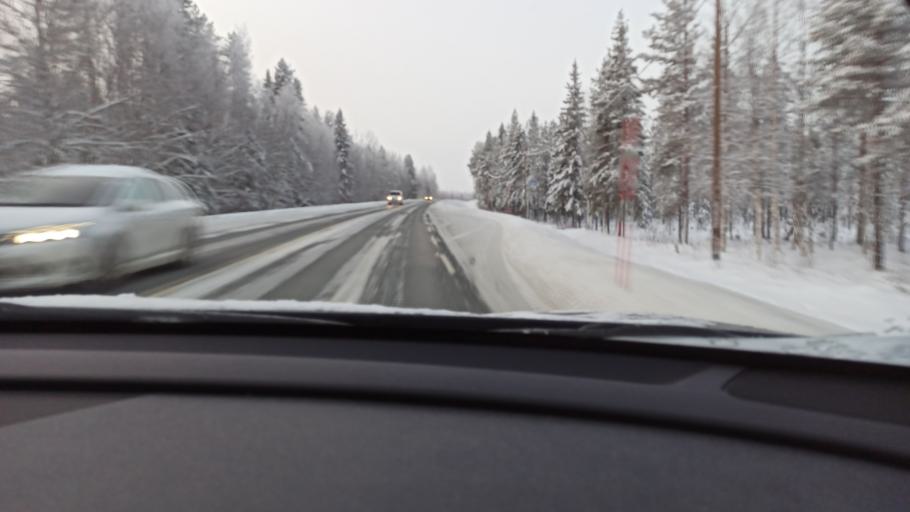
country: FI
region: Lapland
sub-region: Rovaniemi
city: Rovaniemi
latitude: 66.5511
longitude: 25.8906
